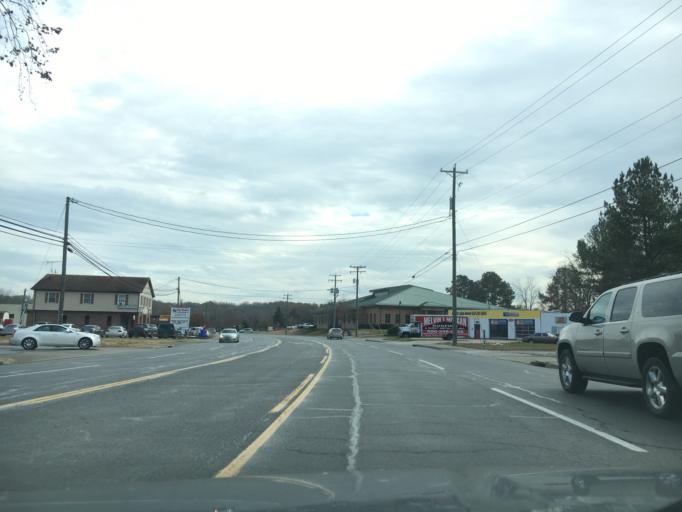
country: US
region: Virginia
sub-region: Prince Edward County
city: Farmville
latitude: 37.3052
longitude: -78.4142
